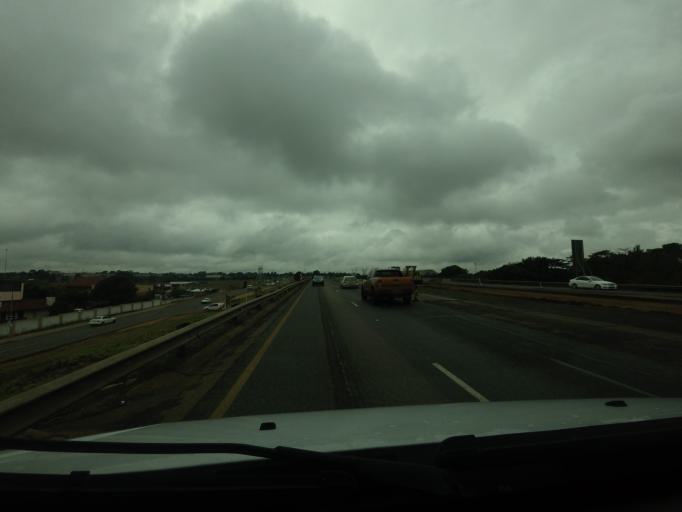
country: ZA
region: Mpumalanga
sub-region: Nkangala District Municipality
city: Witbank
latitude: -25.8839
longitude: 29.1953
